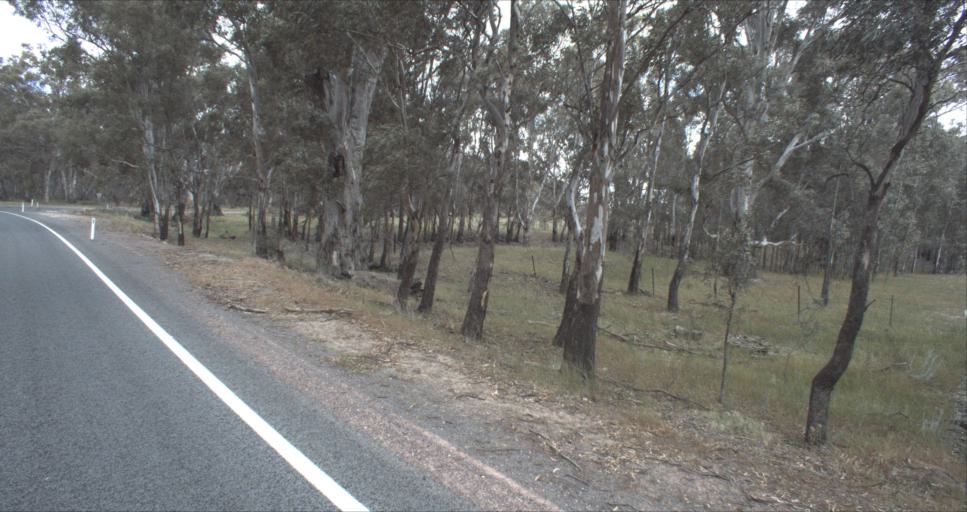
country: AU
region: New South Wales
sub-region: Leeton
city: Leeton
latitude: -34.6412
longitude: 146.3668
